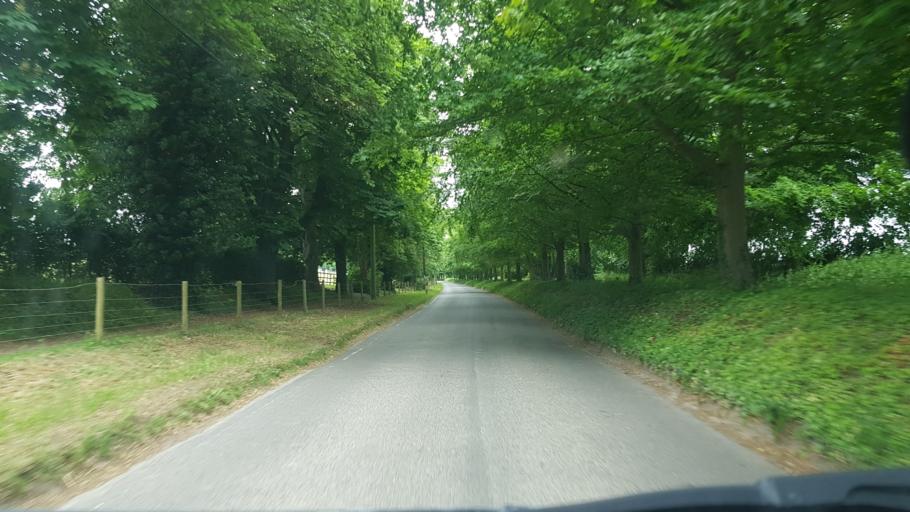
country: GB
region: England
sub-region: Surrey
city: Great Bookham
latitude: 51.2708
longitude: -0.3671
